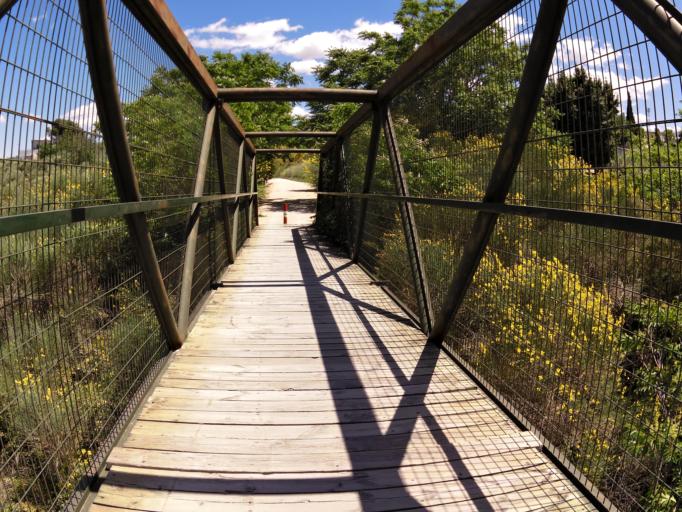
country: ES
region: Andalusia
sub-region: Provincia de Jaen
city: Torredonjimeno
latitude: 37.7539
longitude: -3.9551
